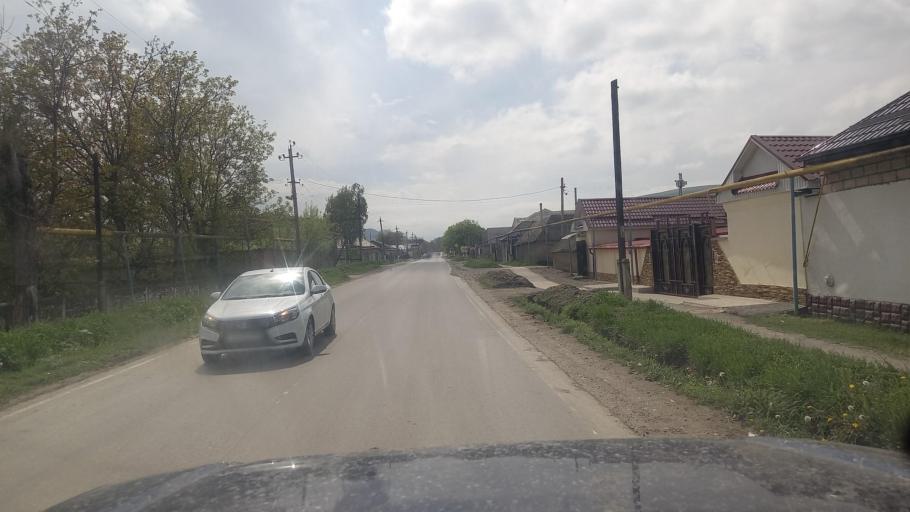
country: RU
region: Kabardino-Balkariya
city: Sarmakovo
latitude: 43.7448
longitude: 43.2022
